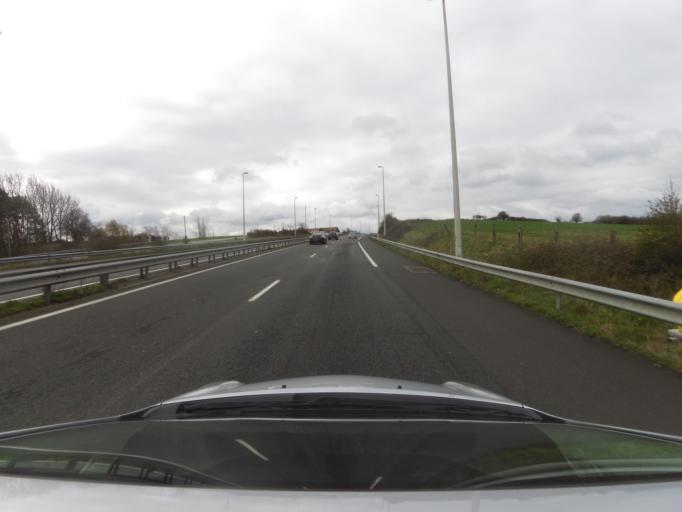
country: FR
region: Nord-Pas-de-Calais
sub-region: Departement du Pas-de-Calais
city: Marquise
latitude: 50.7961
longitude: 1.6882
